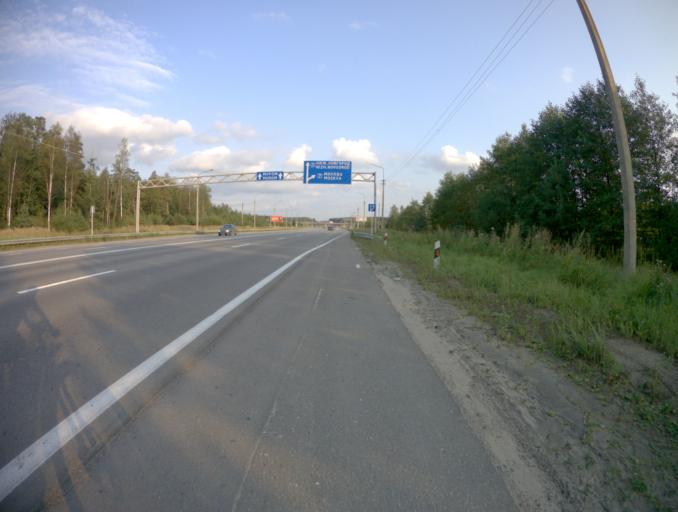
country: RU
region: Vladimir
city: Kommunar
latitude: 56.0831
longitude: 40.4660
